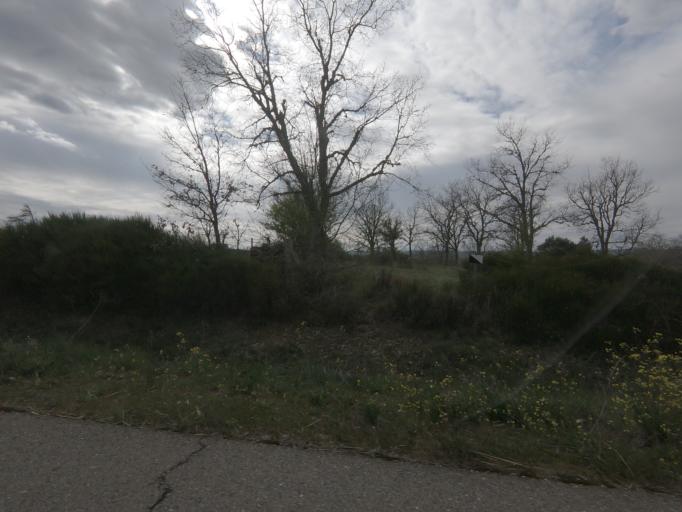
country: ES
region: Castille and Leon
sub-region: Provincia de Salamanca
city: Robleda
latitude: 40.4082
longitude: -6.6037
